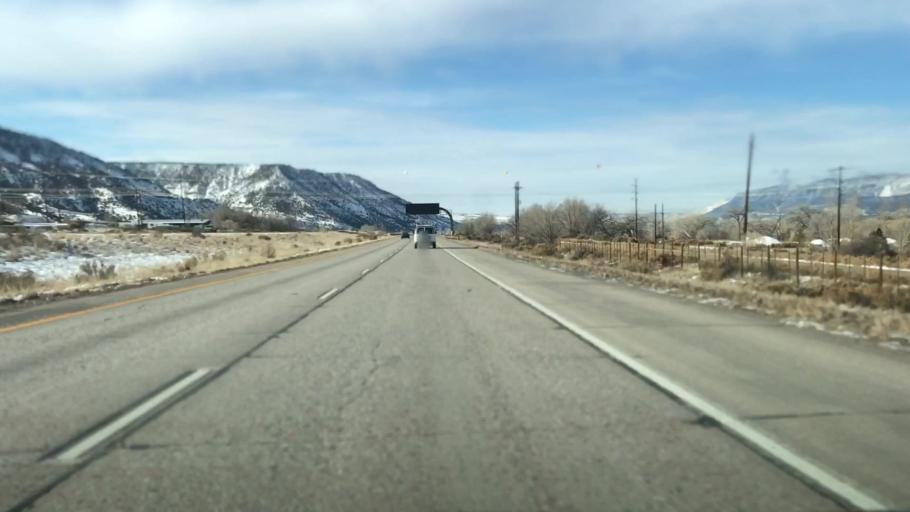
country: US
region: Colorado
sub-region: Garfield County
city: Rifle
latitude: 39.5289
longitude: -107.7429
